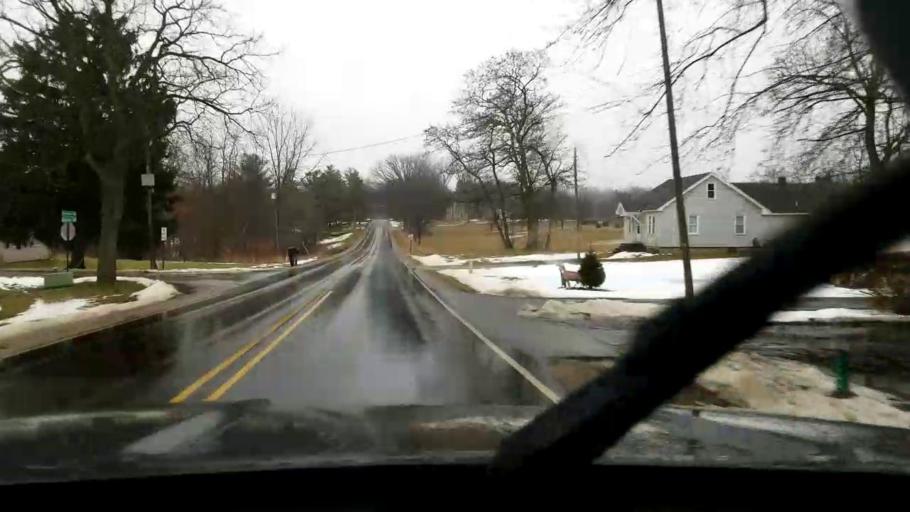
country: US
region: Michigan
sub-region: Jackson County
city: Jackson
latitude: 42.2841
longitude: -84.3605
